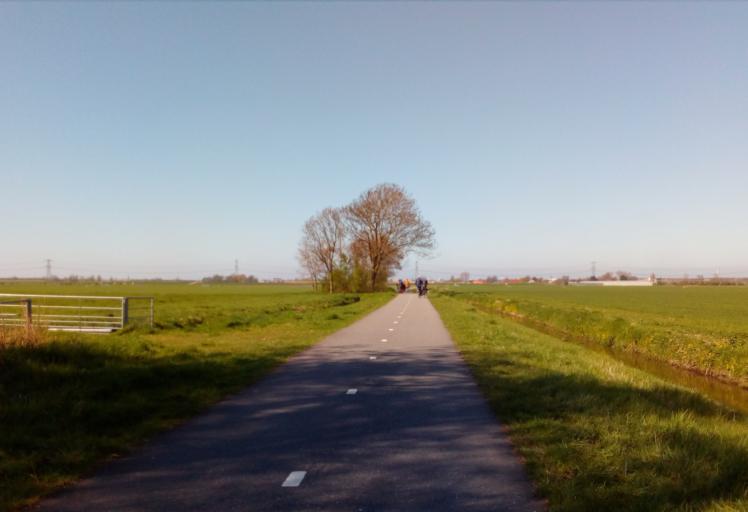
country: NL
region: South Holland
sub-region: Gemeente Westland
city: Kwintsheul
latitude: 51.9968
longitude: 4.2953
